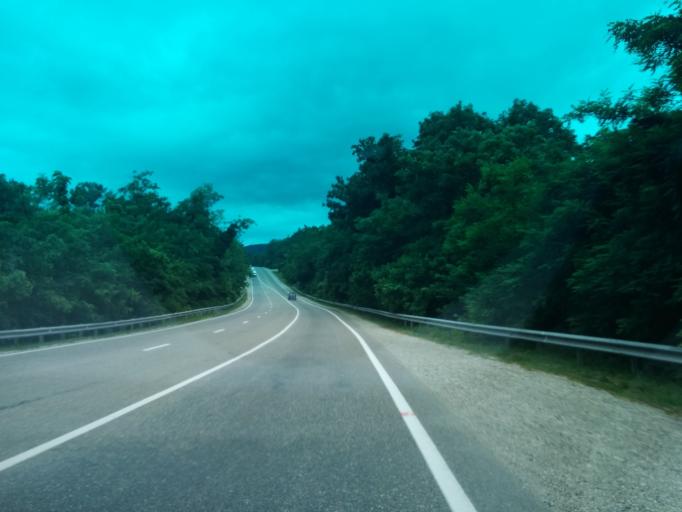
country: RU
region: Krasnodarskiy
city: Ol'ginka
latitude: 44.1778
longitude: 38.9414
